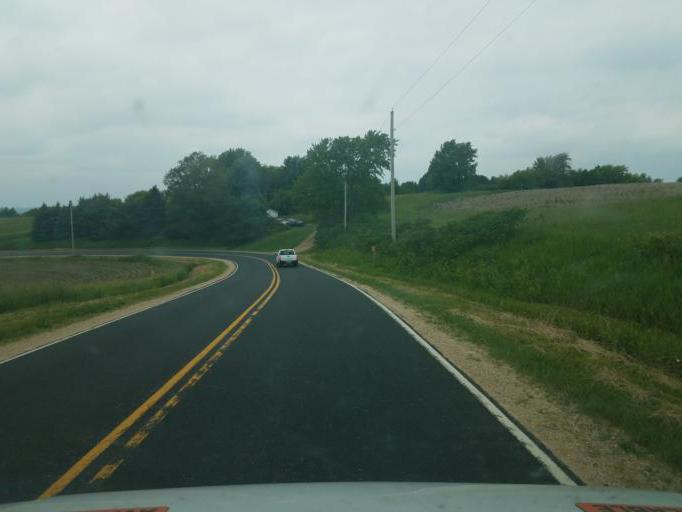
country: US
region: Wisconsin
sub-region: Vernon County
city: Hillsboro
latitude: 43.6520
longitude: -90.3205
